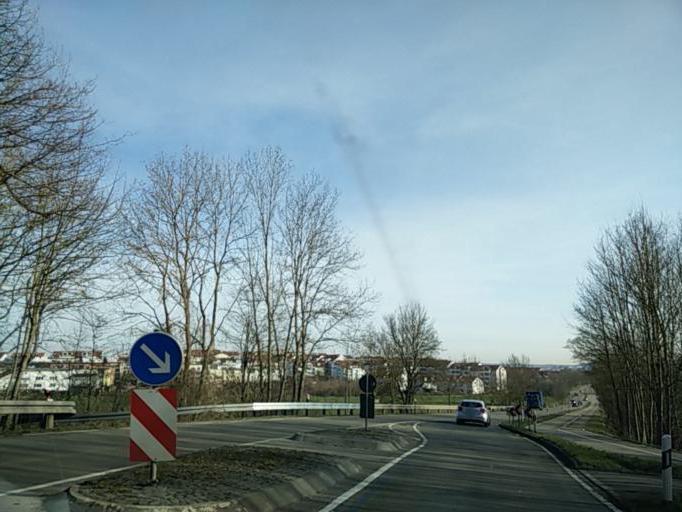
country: DE
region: Baden-Wuerttemberg
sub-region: Regierungsbezirk Stuttgart
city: Boeblingen
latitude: 48.6627
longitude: 9.0056
